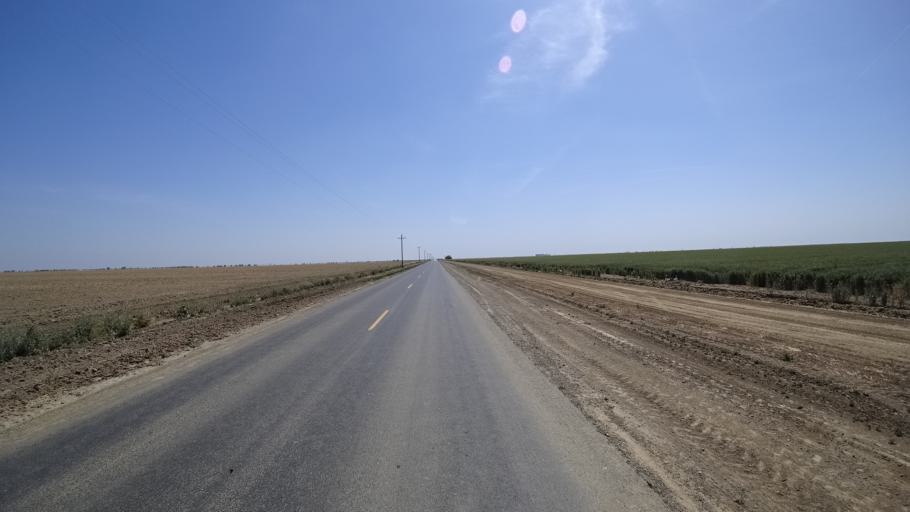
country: US
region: California
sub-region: Kings County
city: Kettleman City
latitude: 36.1377
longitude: -119.9487
